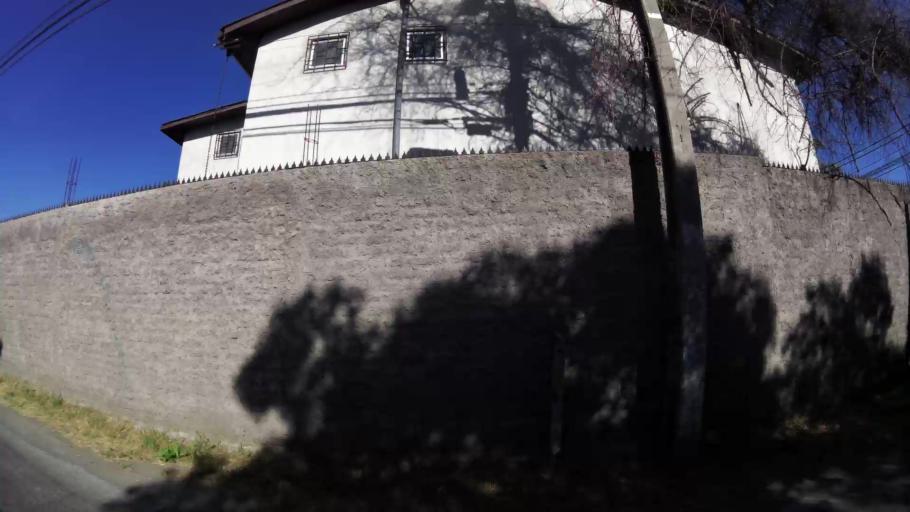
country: CL
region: Santiago Metropolitan
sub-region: Provincia de Santiago
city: La Pintana
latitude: -33.5423
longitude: -70.6713
